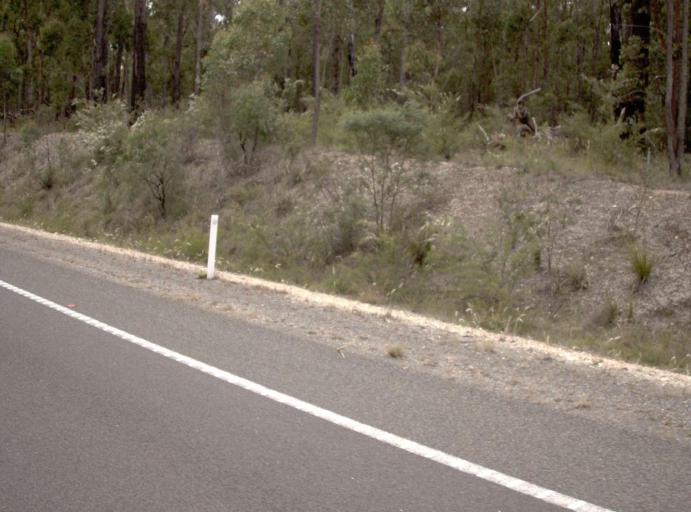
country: AU
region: Victoria
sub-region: East Gippsland
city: Lakes Entrance
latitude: -37.7079
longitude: 147.9900
